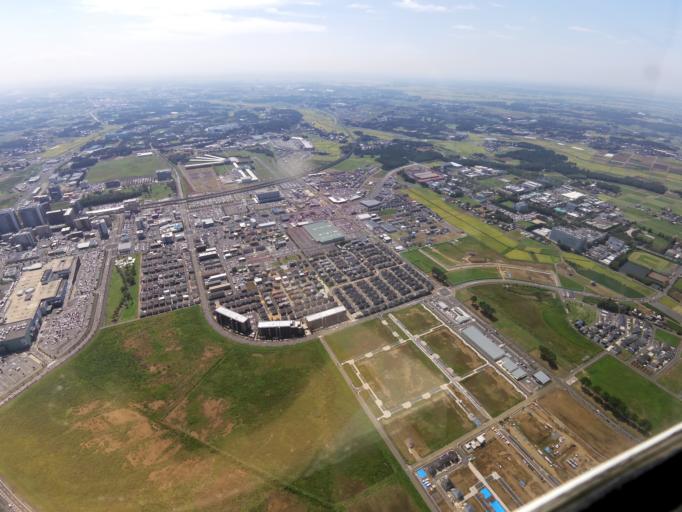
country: JP
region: Ibaraki
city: Naka
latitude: 36.0940
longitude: 140.0808
